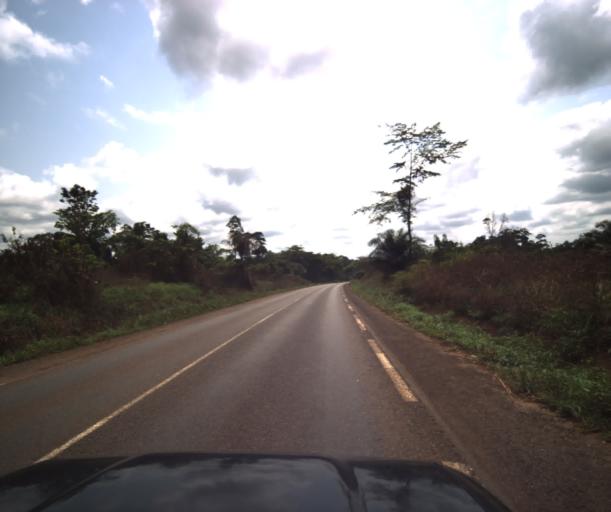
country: CM
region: Centre
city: Eseka
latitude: 3.8920
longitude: 10.7776
